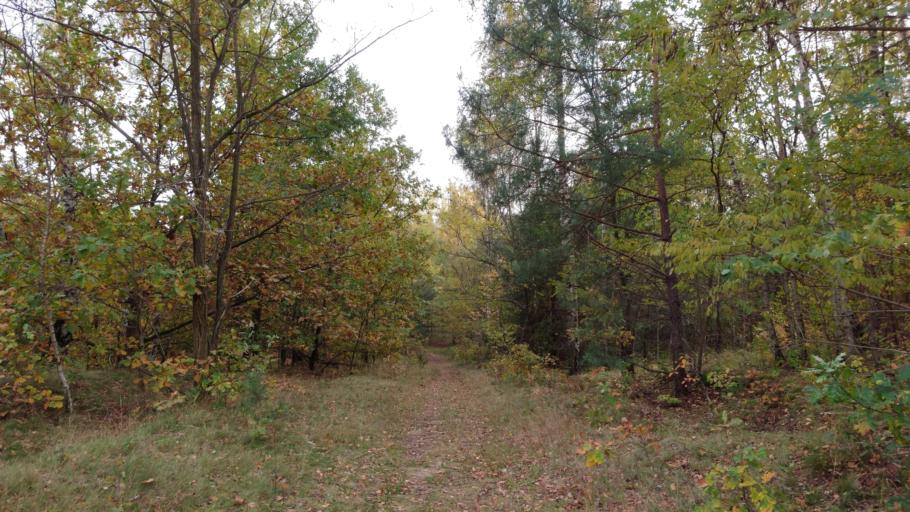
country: DE
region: Saxony
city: Albertstadt
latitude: 51.1023
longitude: 13.7527
